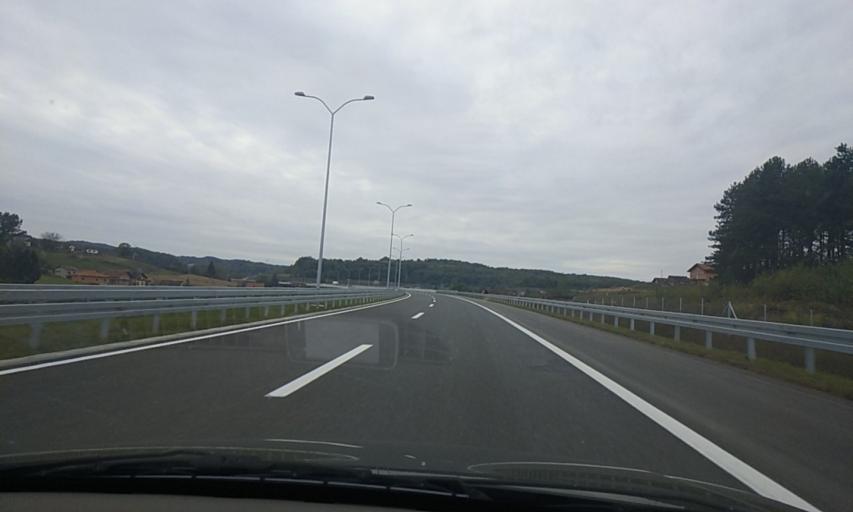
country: BA
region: Republika Srpska
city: Prnjavor
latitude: 44.8814
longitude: 17.5352
